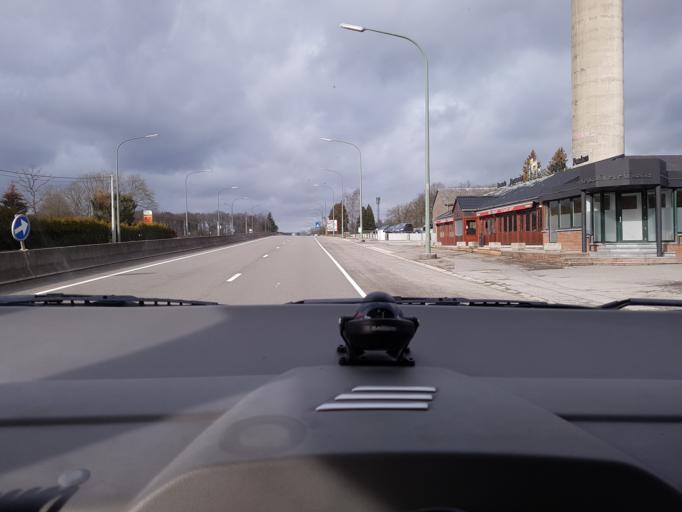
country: BE
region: Wallonia
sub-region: Province du Luxembourg
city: Marche-en-Famenne
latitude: 50.2358
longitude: 5.3009
